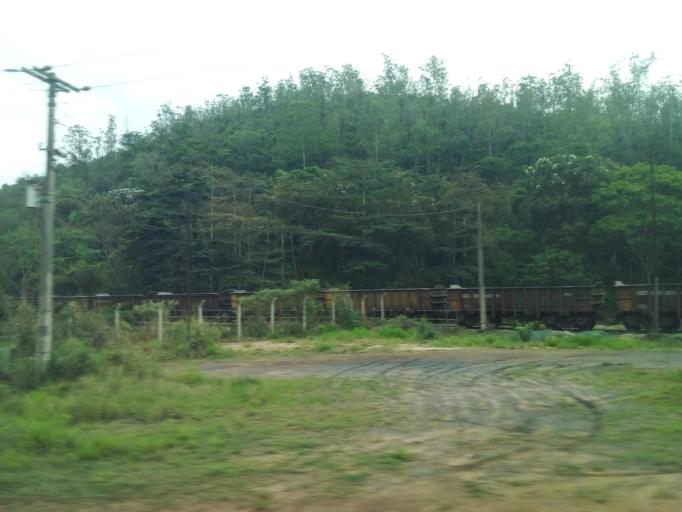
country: BR
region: Minas Gerais
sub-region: Rio Piracicaba
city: Rio Piracicaba
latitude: -19.9463
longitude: -43.1892
